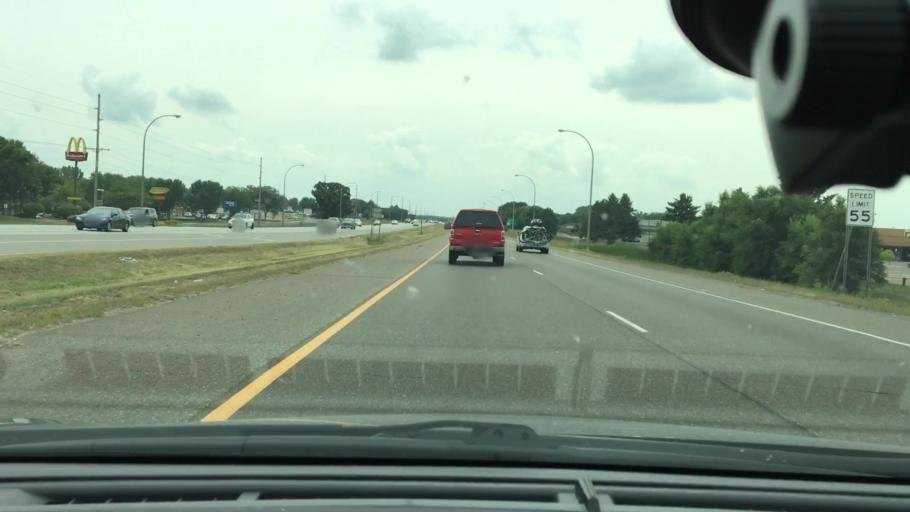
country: US
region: Minnesota
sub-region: Sherburne County
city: Elk River
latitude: 45.3114
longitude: -93.5584
